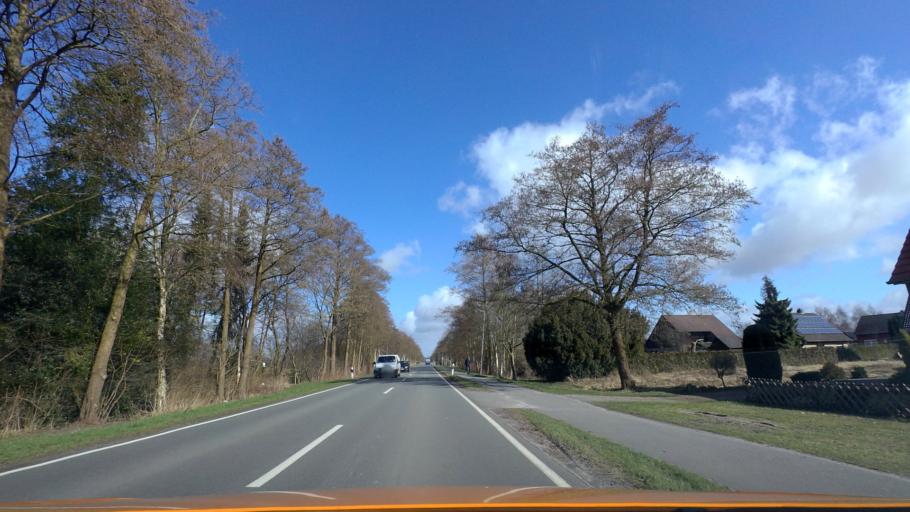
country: DE
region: Lower Saxony
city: Edewecht
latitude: 53.0896
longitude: 7.9416
